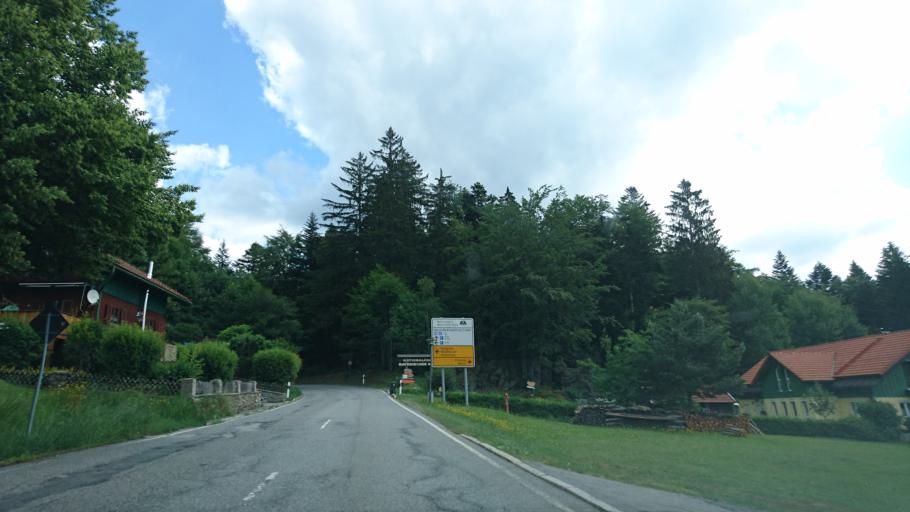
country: DE
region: Bavaria
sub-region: Lower Bavaria
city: Neuschonau
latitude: 48.8889
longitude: 13.4885
